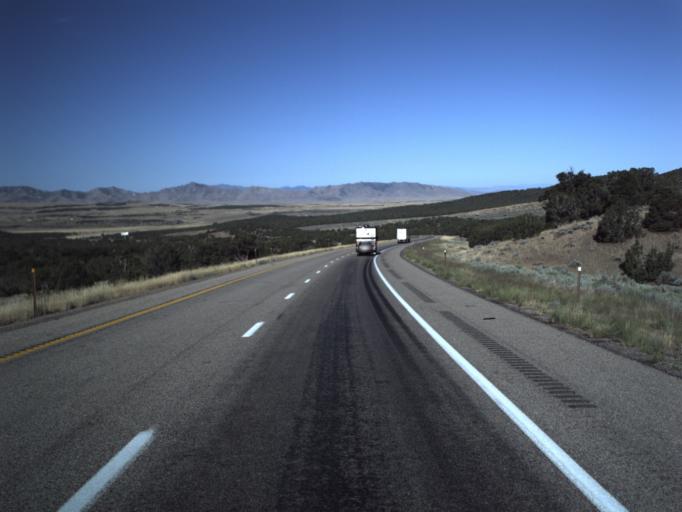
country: US
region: Utah
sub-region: Beaver County
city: Beaver
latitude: 38.6050
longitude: -112.5355
